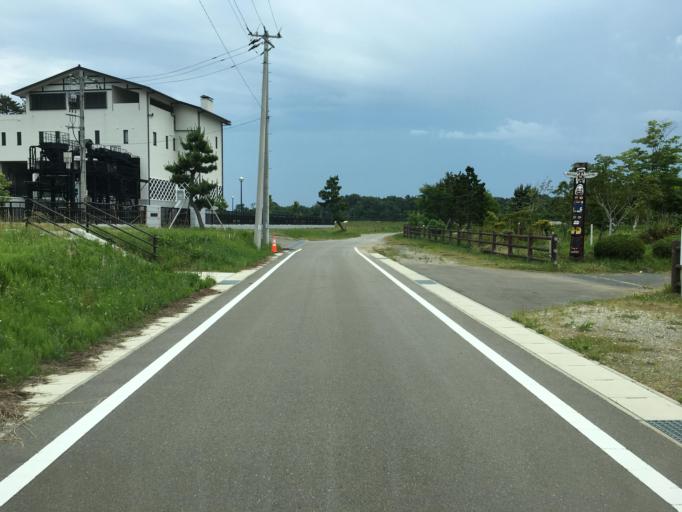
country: JP
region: Miyagi
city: Marumori
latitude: 37.8217
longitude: 140.9504
